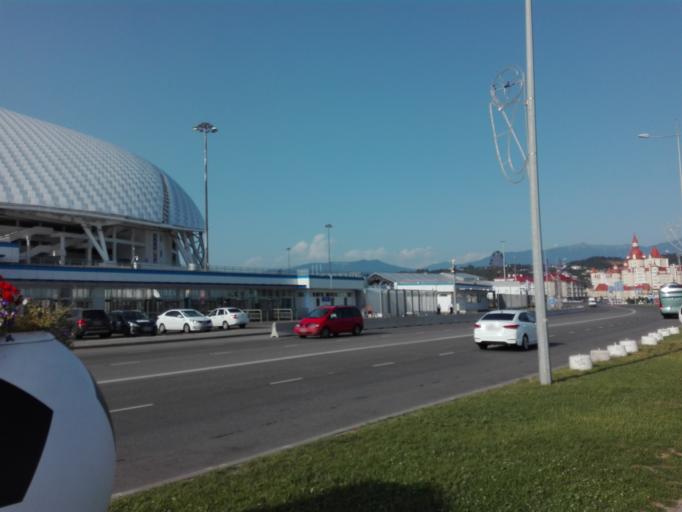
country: RU
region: Krasnodarskiy
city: Adler
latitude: 43.3999
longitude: 39.9569
